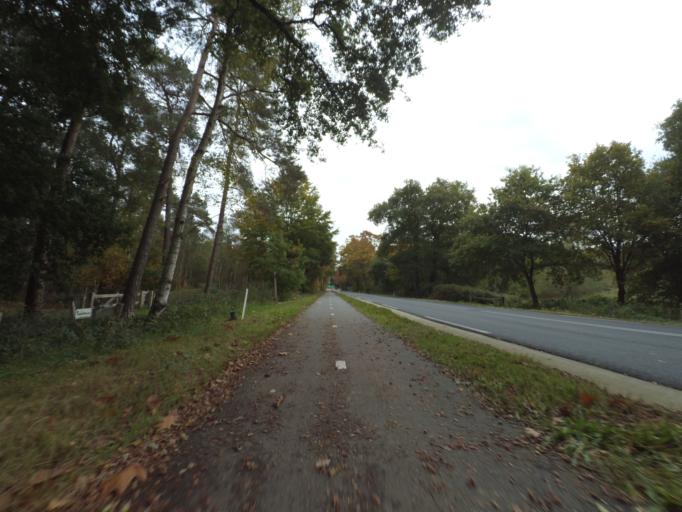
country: NL
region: Gelderland
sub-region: Gemeente Ermelo
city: Ermelo
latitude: 52.3043
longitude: 5.6758
